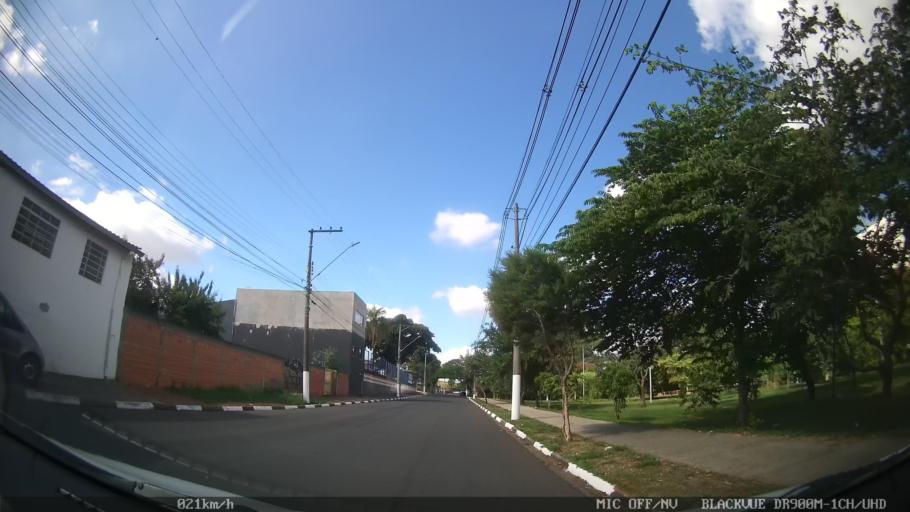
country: BR
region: Sao Paulo
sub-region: Hortolandia
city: Hortolandia
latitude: -22.8966
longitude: -47.1932
